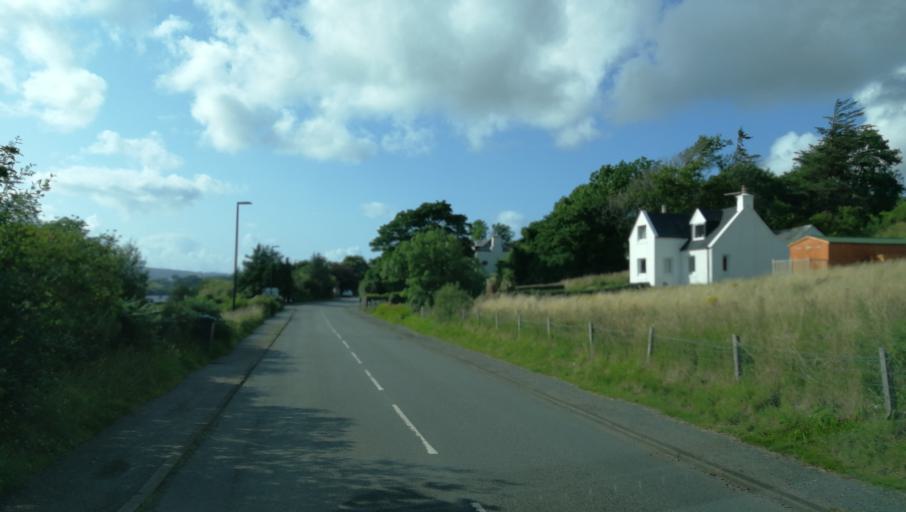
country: GB
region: Scotland
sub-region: Highland
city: Isle of Skye
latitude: 57.4345
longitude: -6.5777
